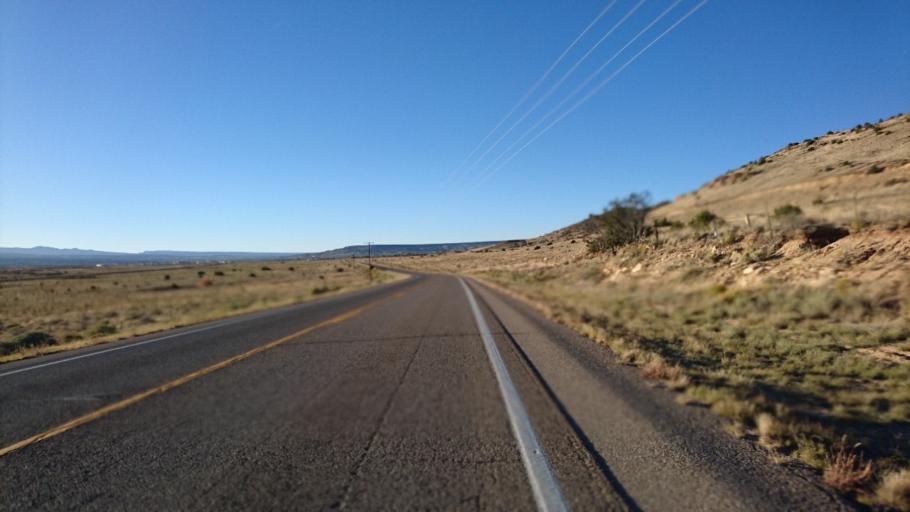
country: US
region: New Mexico
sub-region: Cibola County
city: Grants
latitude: 35.1135
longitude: -107.7839
